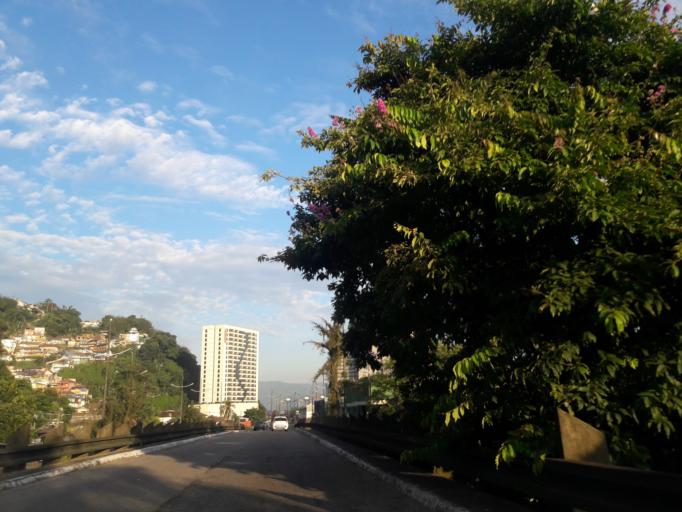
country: BR
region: Sao Paulo
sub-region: Santos
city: Santos
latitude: -23.9347
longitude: -46.3349
